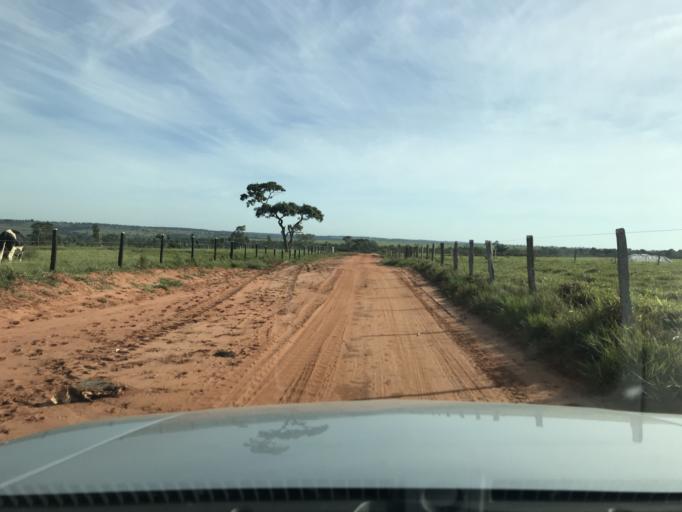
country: BR
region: Mato Grosso do Sul
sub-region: Iguatemi
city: Iguatemi
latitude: -23.6534
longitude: -54.5736
